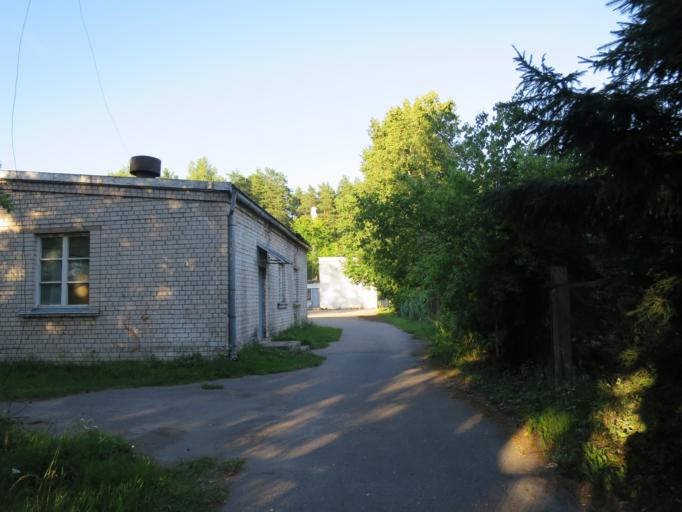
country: LV
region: Riga
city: Bergi
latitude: 56.9772
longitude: 24.3102
